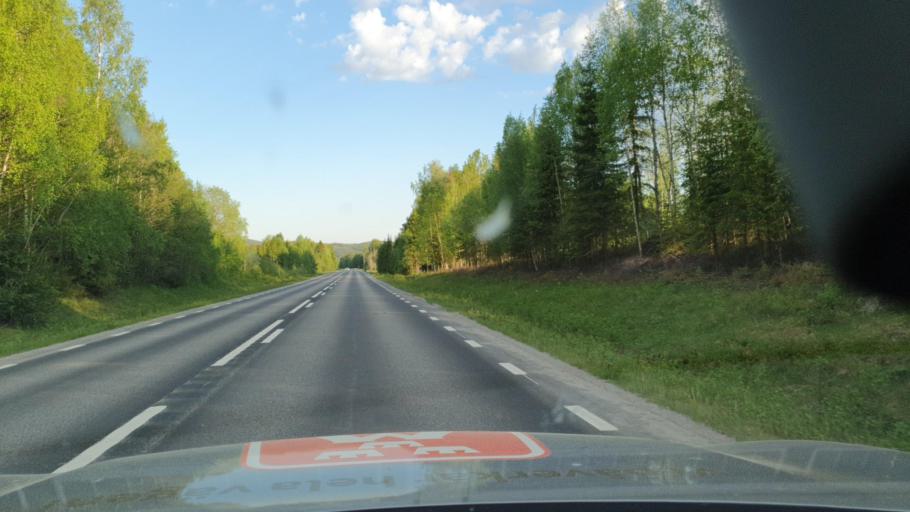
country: SE
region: Vaesternorrland
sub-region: Solleftea Kommun
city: As
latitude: 63.6300
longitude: 16.8147
